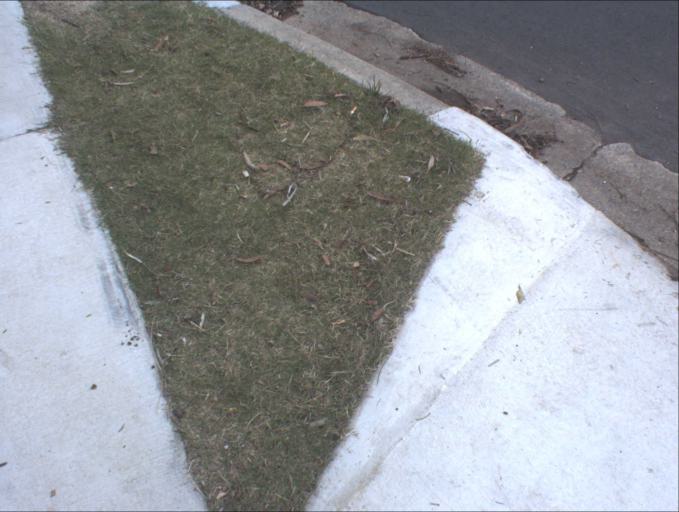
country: AU
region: Queensland
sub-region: Logan
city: Waterford West
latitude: -27.6723
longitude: 153.1425
